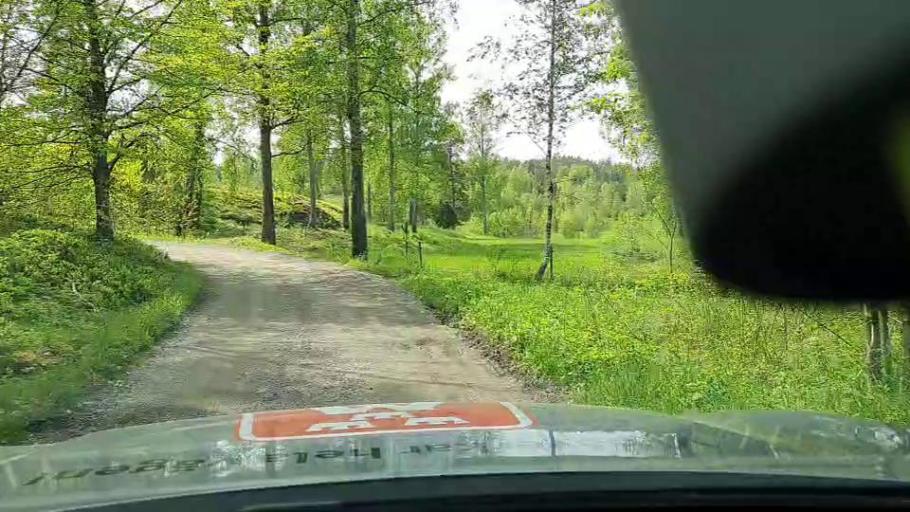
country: SE
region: Soedermanland
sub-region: Eskilstuna Kommun
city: Skogstorp
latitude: 59.2519
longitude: 16.5016
